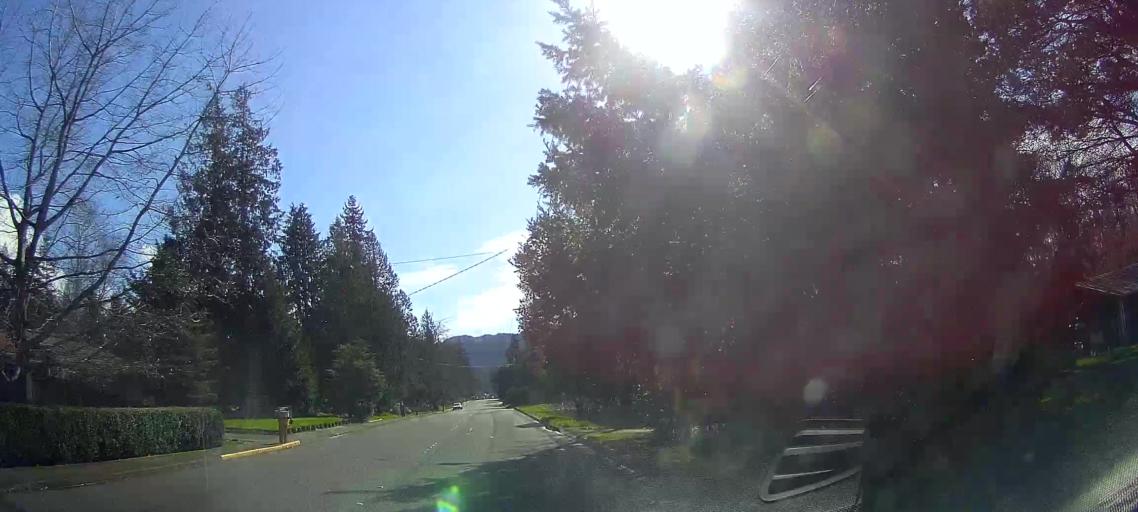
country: US
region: Washington
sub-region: Whatcom County
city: Bellingham
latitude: 48.7236
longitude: -122.4754
